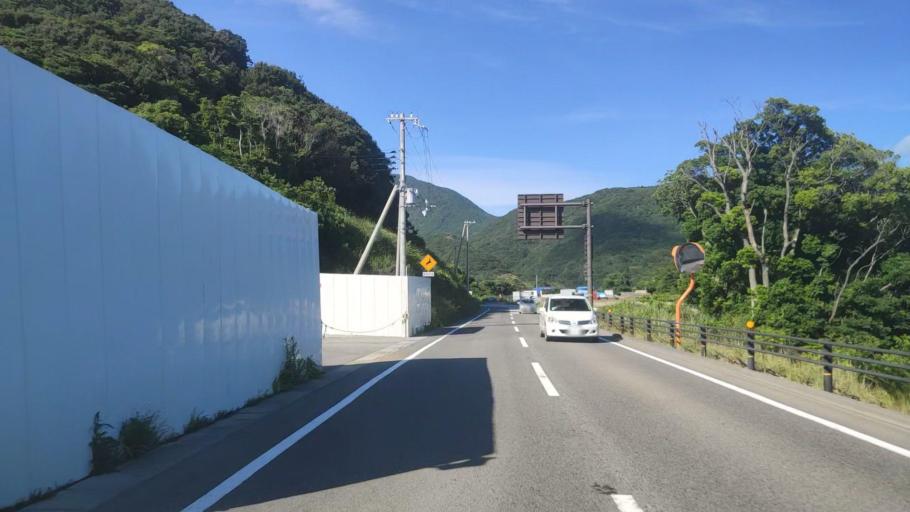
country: JP
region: Wakayama
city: Tanabe
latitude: 33.5090
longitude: 135.6015
